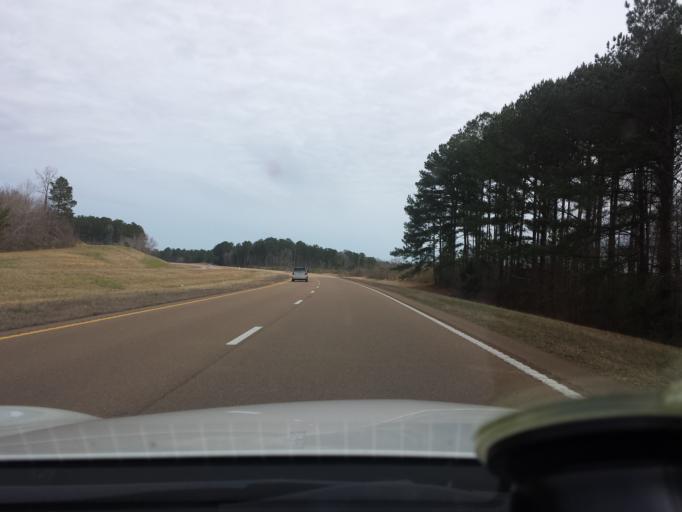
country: US
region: Mississippi
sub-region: Leake County
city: Carthage
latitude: 32.5925
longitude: -89.7054
